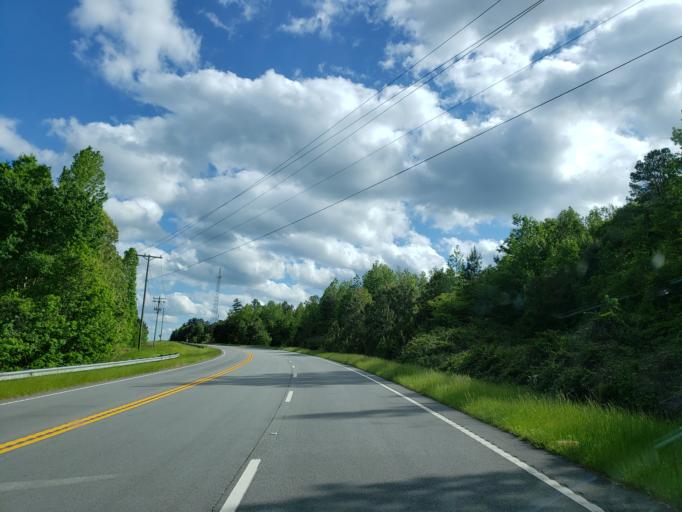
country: US
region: Georgia
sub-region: Carroll County
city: Mount Zion
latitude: 33.6409
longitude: -85.2774
